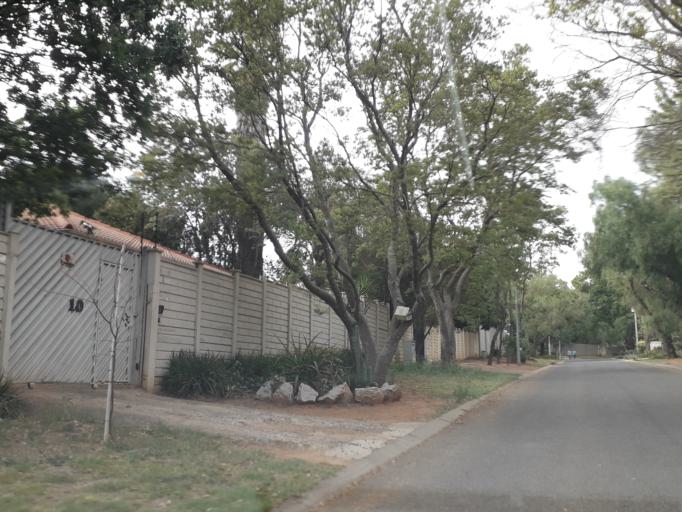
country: ZA
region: Gauteng
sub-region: City of Johannesburg Metropolitan Municipality
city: Roodepoort
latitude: -26.1033
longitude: 27.9593
